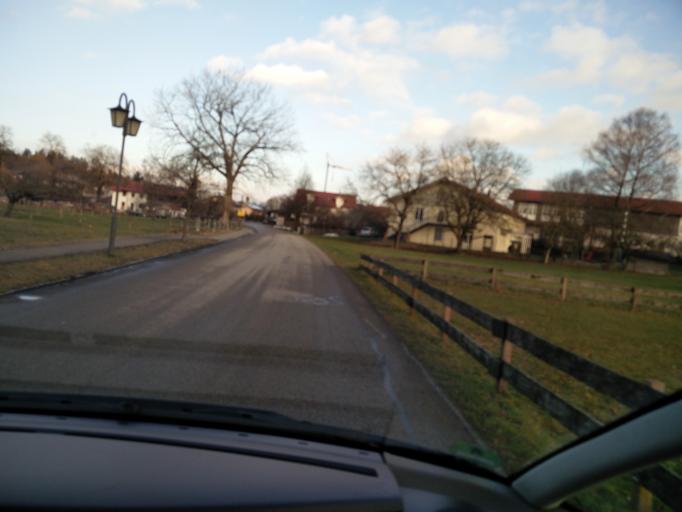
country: DE
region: Bavaria
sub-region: Upper Bavaria
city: Hoslwang
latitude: 47.9541
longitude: 12.3272
